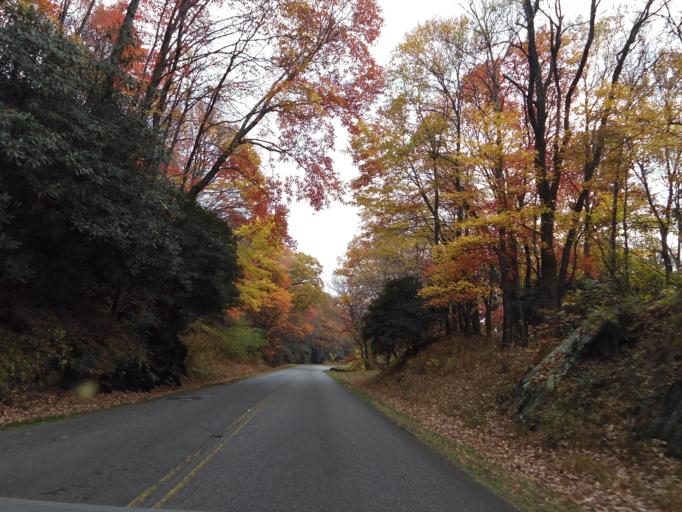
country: US
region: North Carolina
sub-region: Alleghany County
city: Sparta
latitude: 36.4274
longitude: -81.1839
